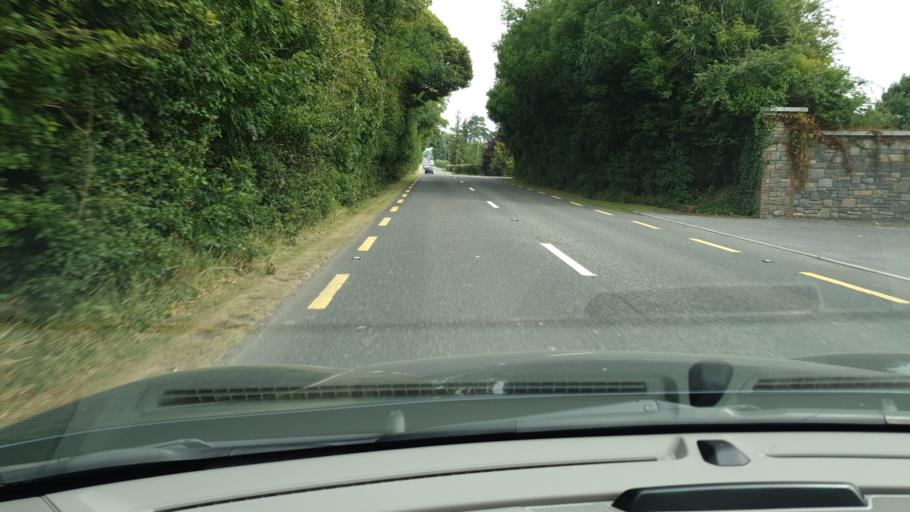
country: IE
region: Leinster
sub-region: An Mhi
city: Athboy
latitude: 53.6734
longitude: -6.9624
